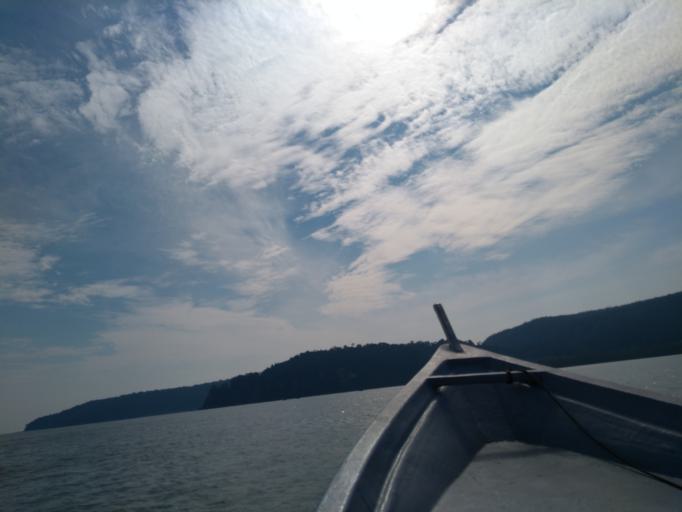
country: MY
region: Sarawak
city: Kuching
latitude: 1.7080
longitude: 110.4318
